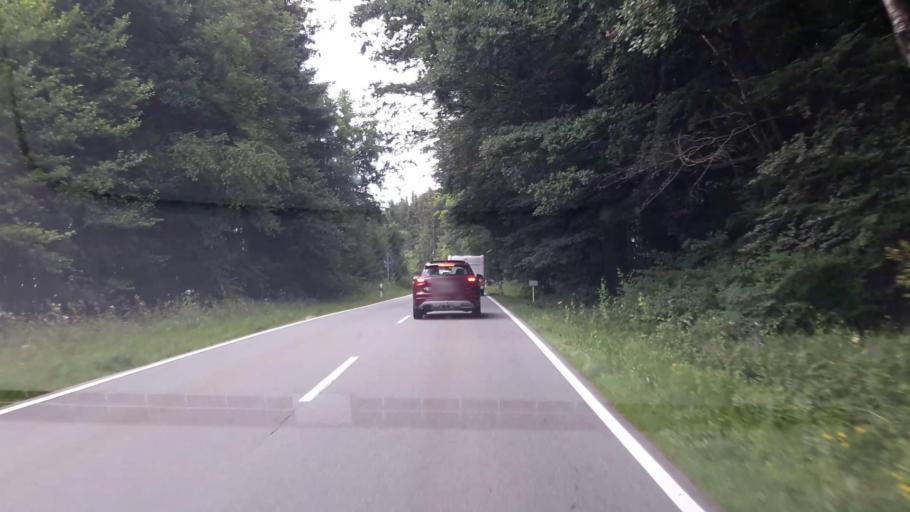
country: DE
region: Bavaria
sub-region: Upper Bavaria
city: Anger
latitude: 47.8090
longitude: 12.8594
